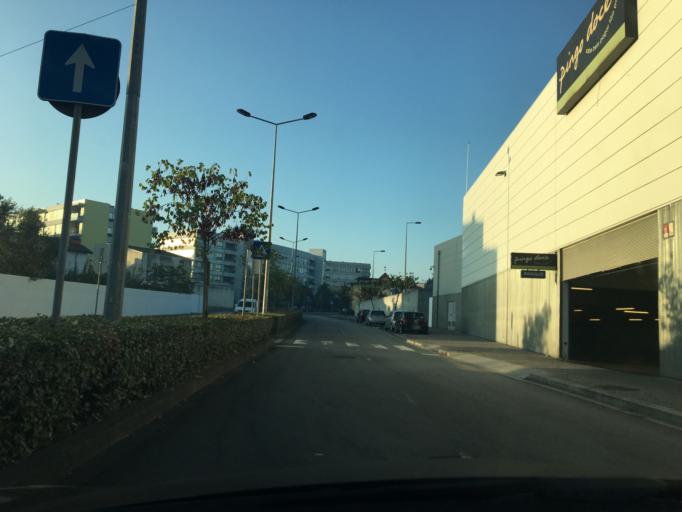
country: PT
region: Porto
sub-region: Maia
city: Anta
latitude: 41.2650
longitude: -8.6147
